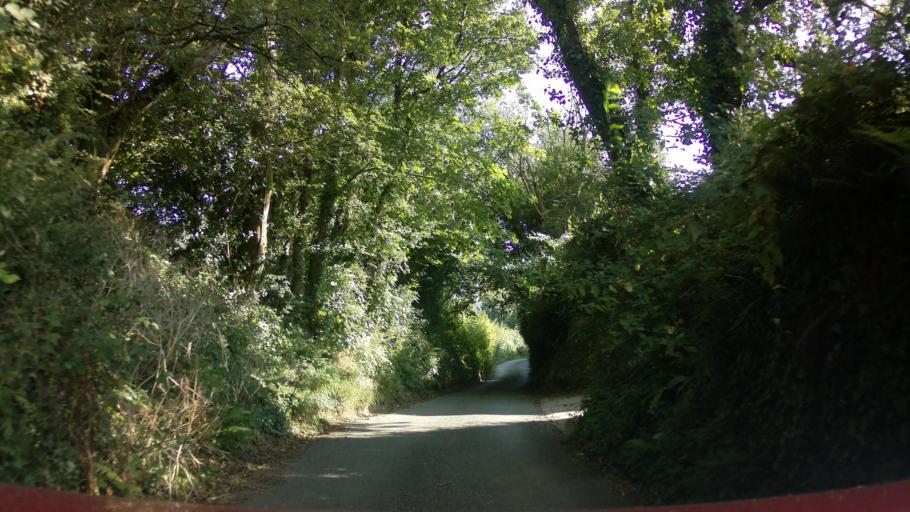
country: GB
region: England
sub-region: Devon
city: Totnes
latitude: 50.4172
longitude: -3.7217
